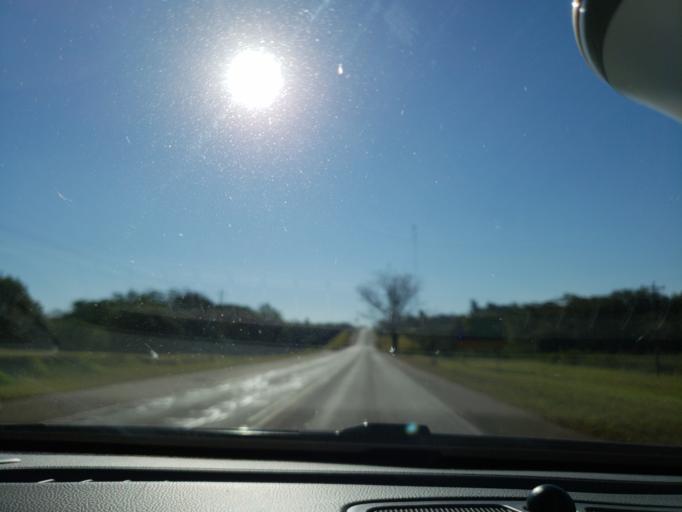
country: AR
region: Misiones
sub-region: Departamento de Apostoles
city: San Jose
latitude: -27.7556
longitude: -55.7756
